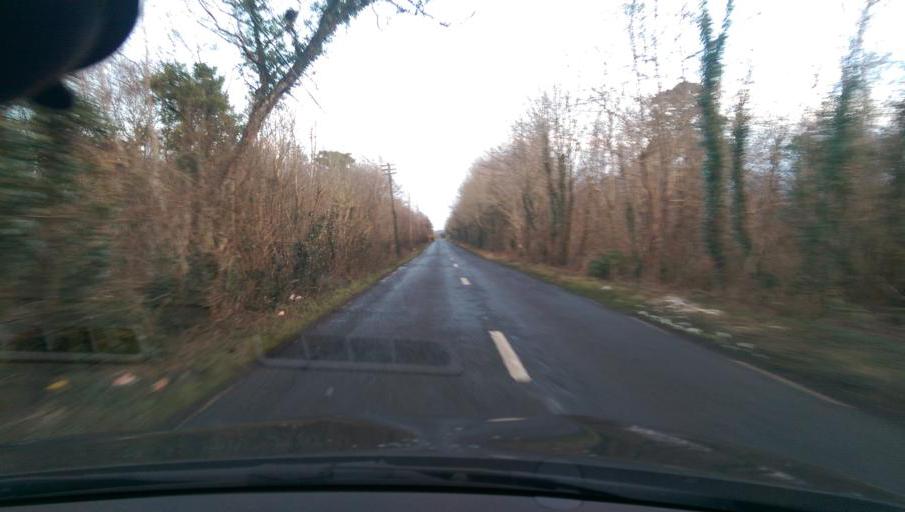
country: IE
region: Connaught
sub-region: County Galway
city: Ballinasloe
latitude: 53.3600
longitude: -8.2578
